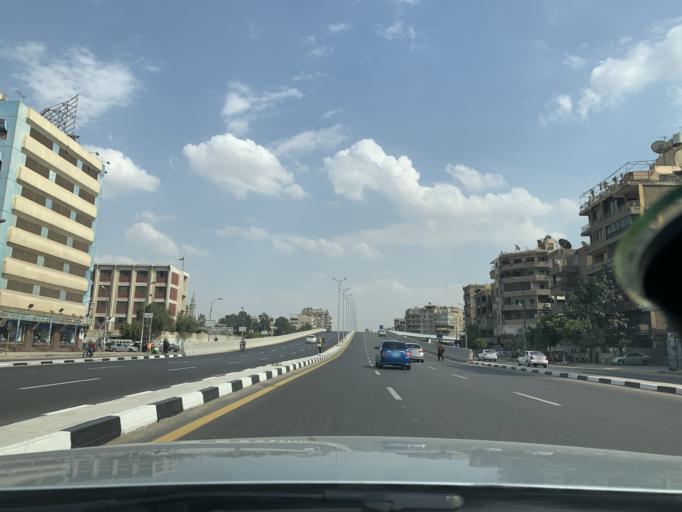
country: EG
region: Muhafazat al Qalyubiyah
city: Al Khankah
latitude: 30.1135
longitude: 31.3443
